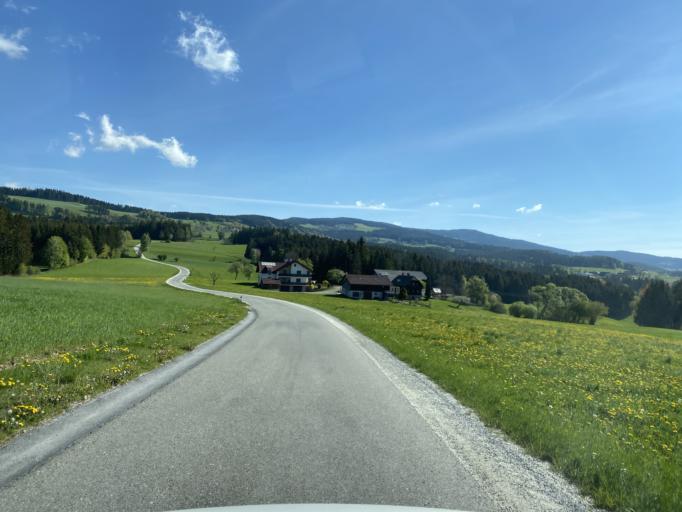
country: AT
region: Styria
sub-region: Politischer Bezirk Weiz
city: Strallegg
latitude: 47.3704
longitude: 15.7154
